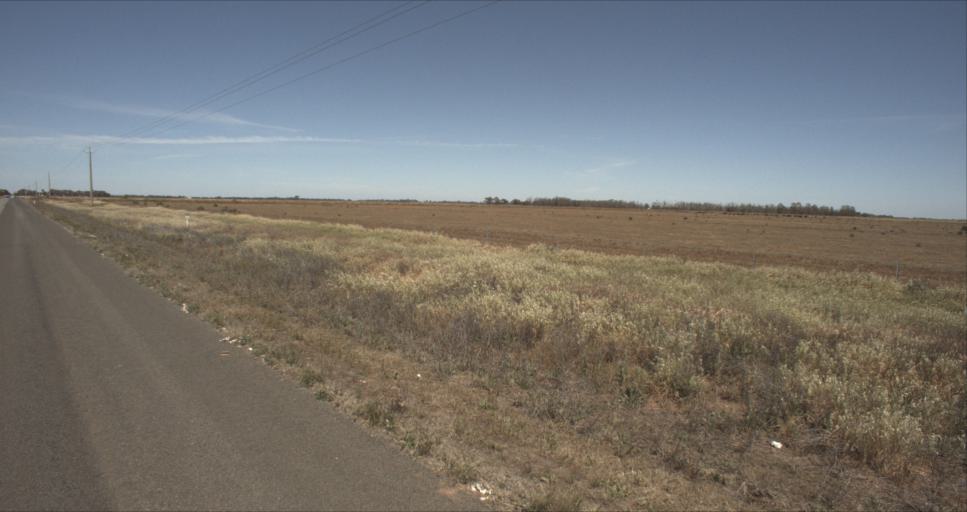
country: AU
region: New South Wales
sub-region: Leeton
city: Leeton
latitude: -34.4799
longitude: 146.2907
